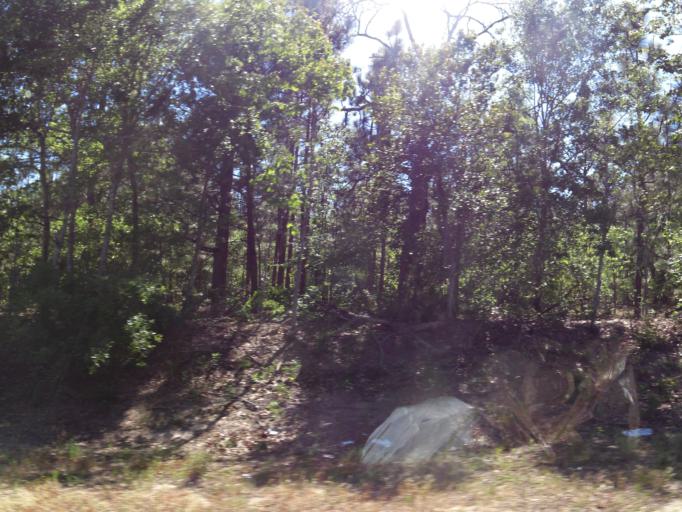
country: US
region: South Carolina
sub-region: Barnwell County
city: Williston
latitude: 33.4607
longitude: -81.4989
